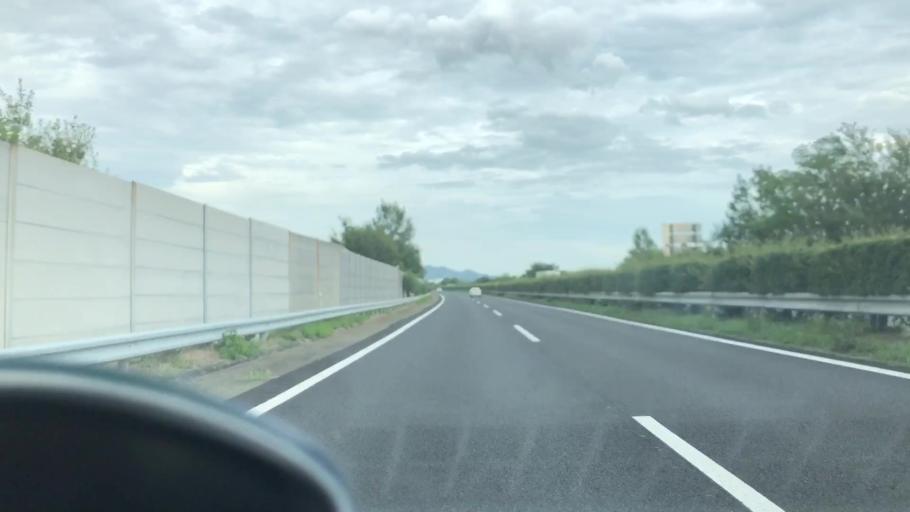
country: JP
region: Hyogo
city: Yashiro
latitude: 34.9289
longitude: 134.9519
